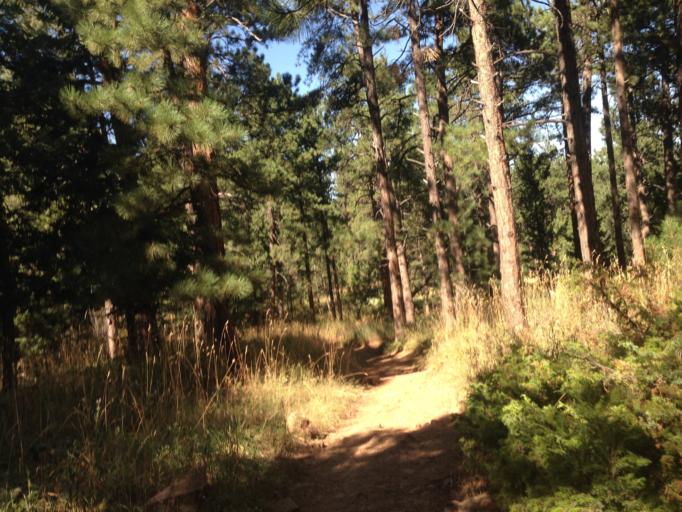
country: US
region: Colorado
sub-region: Boulder County
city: Boulder
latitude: 39.9868
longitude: -105.2861
